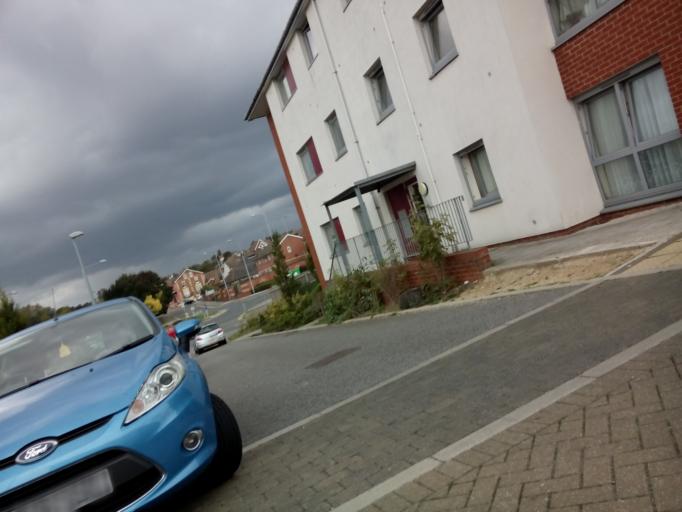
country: GB
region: England
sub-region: Suffolk
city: Ipswich
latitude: 52.0449
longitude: 1.1568
